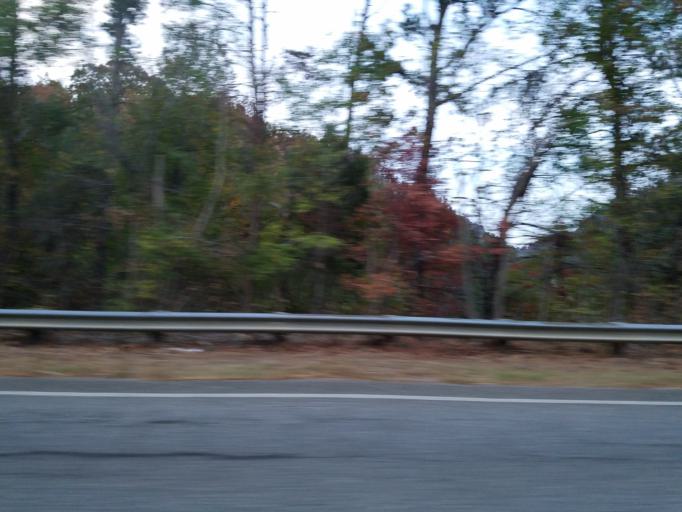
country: US
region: Georgia
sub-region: Murray County
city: Chatsworth
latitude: 34.5888
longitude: -84.6661
